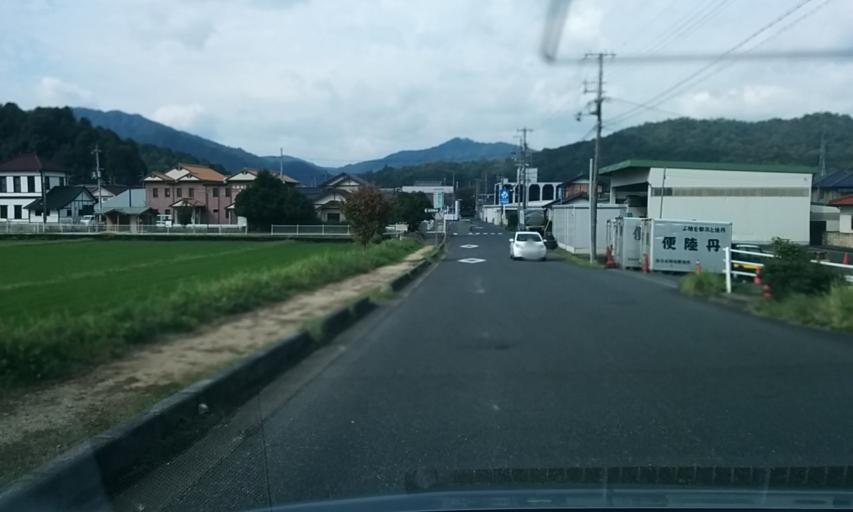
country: JP
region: Kyoto
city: Miyazu
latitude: 35.5046
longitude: 135.0962
